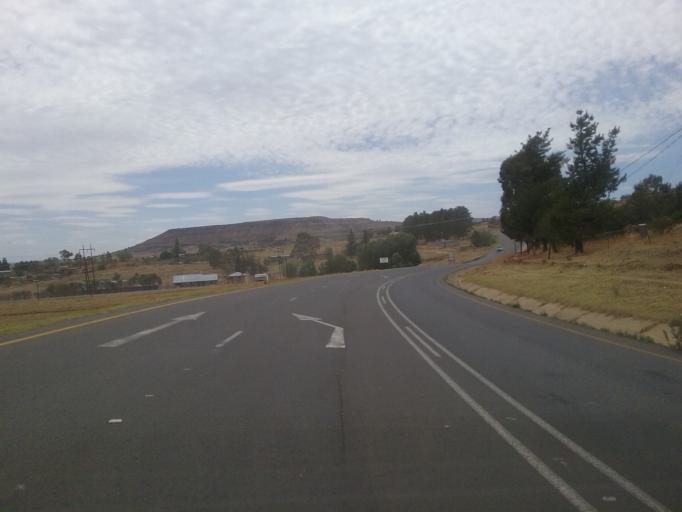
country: LS
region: Maseru
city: Nako
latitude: -29.6311
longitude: 27.4823
